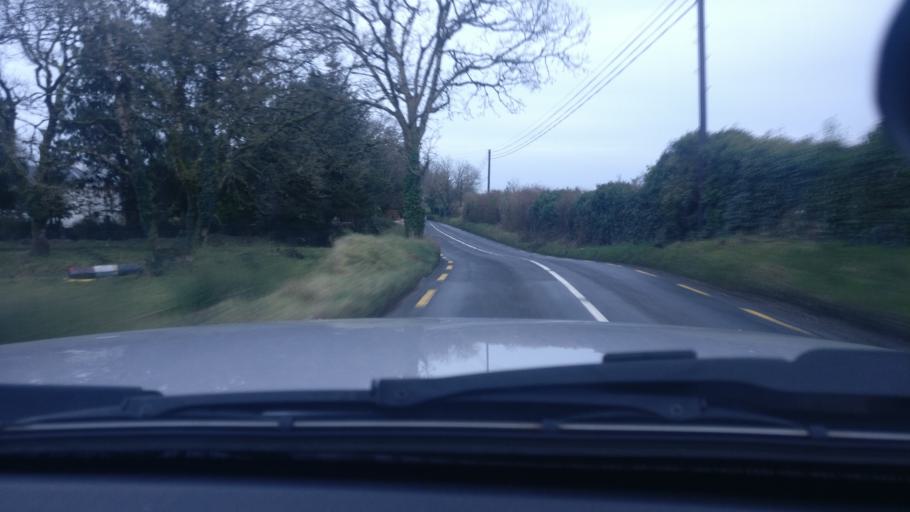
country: IE
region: Connaught
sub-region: County Galway
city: Loughrea
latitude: 53.1614
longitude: -8.5172
